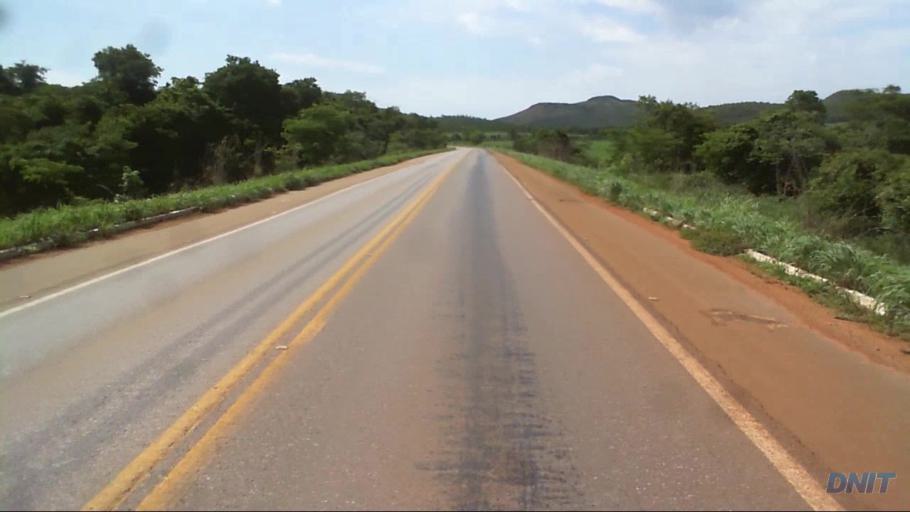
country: BR
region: Goias
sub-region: Barro Alto
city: Barro Alto
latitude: -15.1268
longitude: -48.8357
